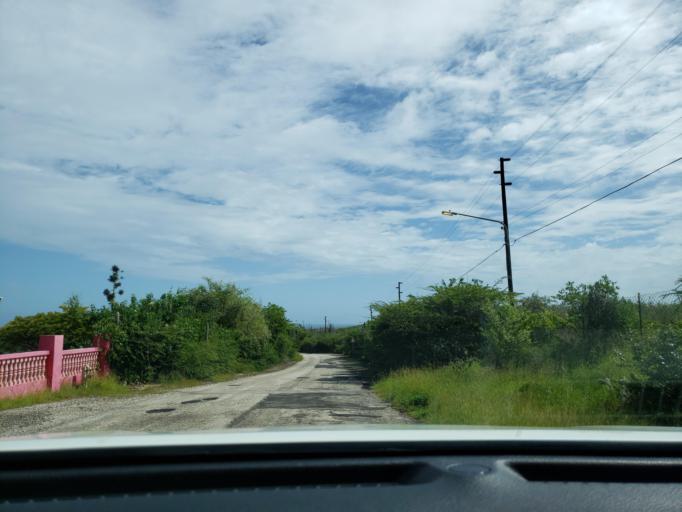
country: CW
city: Barber
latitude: 12.3148
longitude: -69.0899
